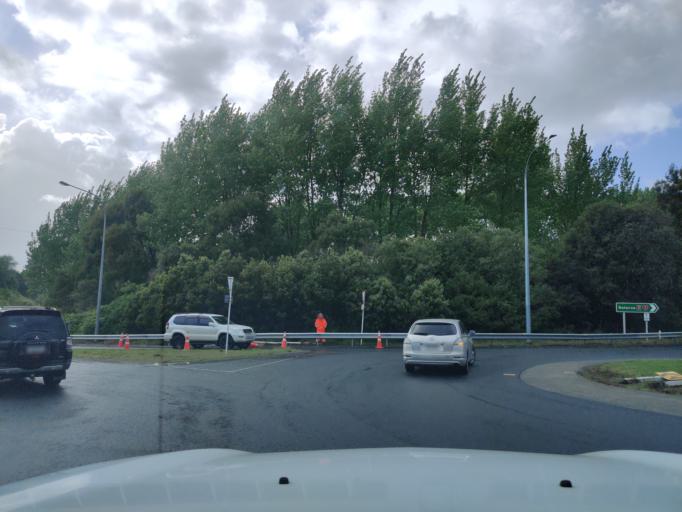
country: NZ
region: Waikato
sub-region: Hamilton City
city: Hamilton
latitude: -37.8278
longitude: 175.3578
